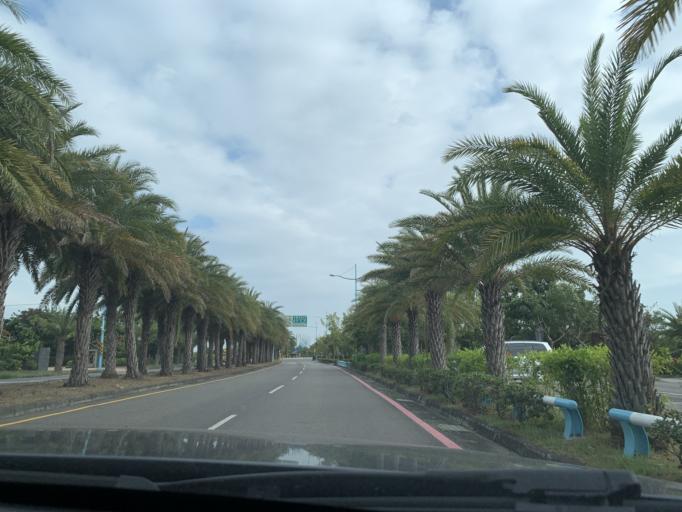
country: TW
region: Taiwan
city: Fengshan
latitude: 22.4423
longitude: 120.4916
